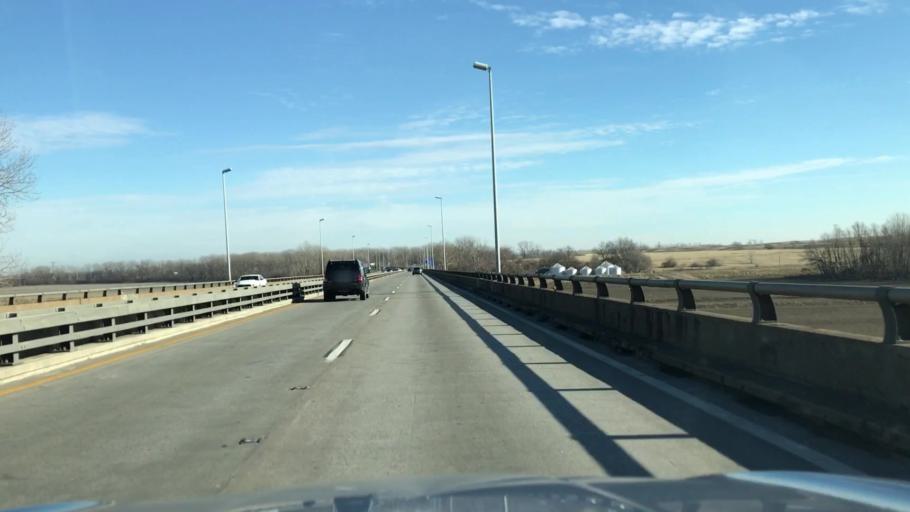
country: US
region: Missouri
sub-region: Saint Louis County
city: Glasgow Village
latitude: 38.7629
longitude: -90.1666
